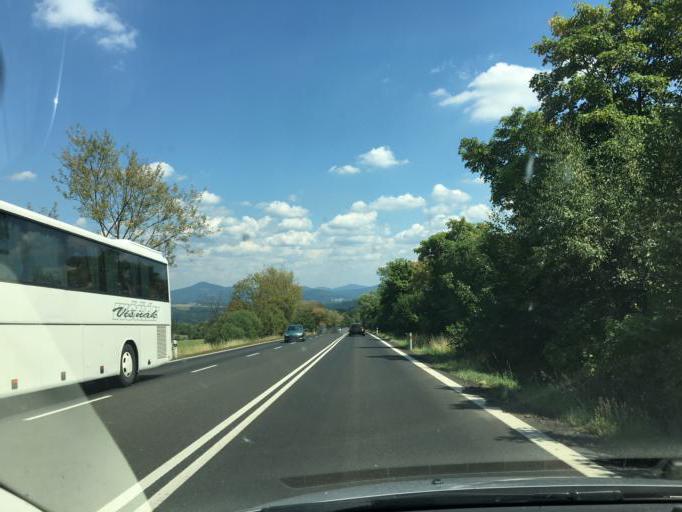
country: CZ
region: Ustecky
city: Benesov nad Ploucnici
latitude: 50.7891
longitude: 14.2924
